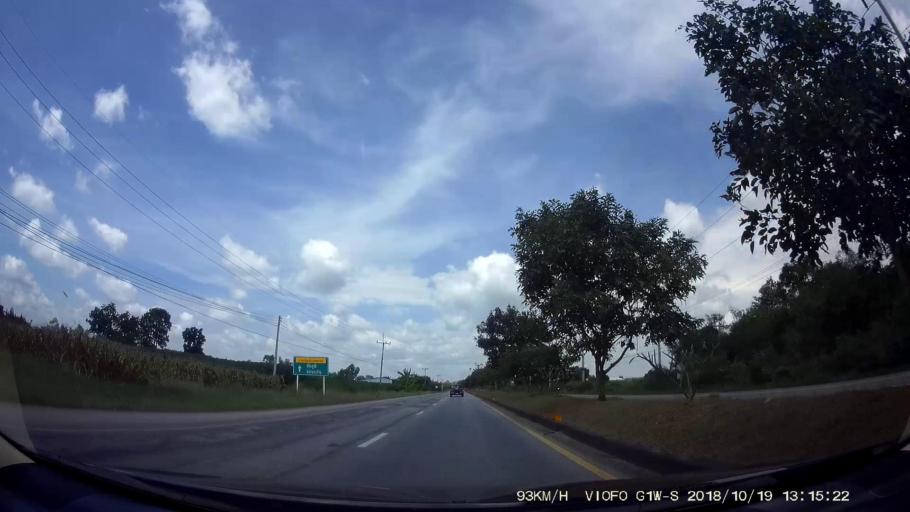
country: TH
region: Chaiyaphum
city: Chatturat
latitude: 15.3887
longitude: 101.8386
